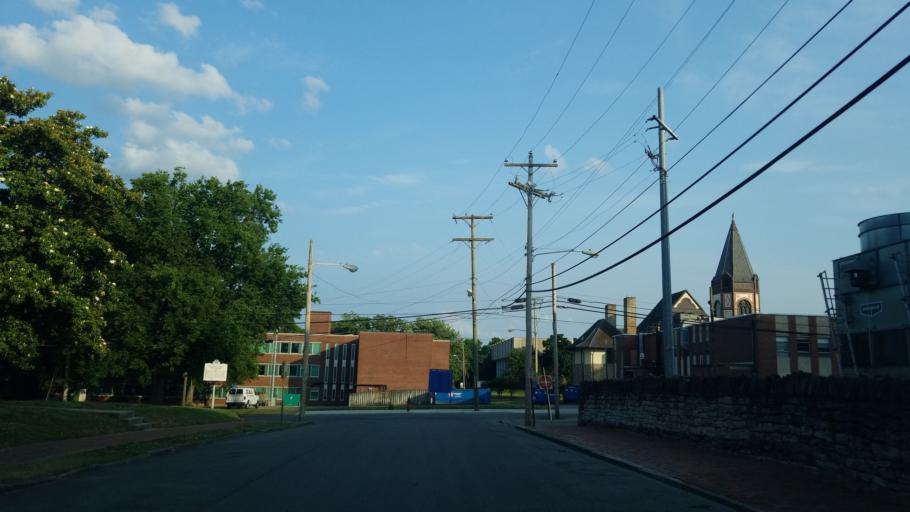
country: US
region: Tennessee
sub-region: Davidson County
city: Nashville
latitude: 36.1690
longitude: -86.8040
